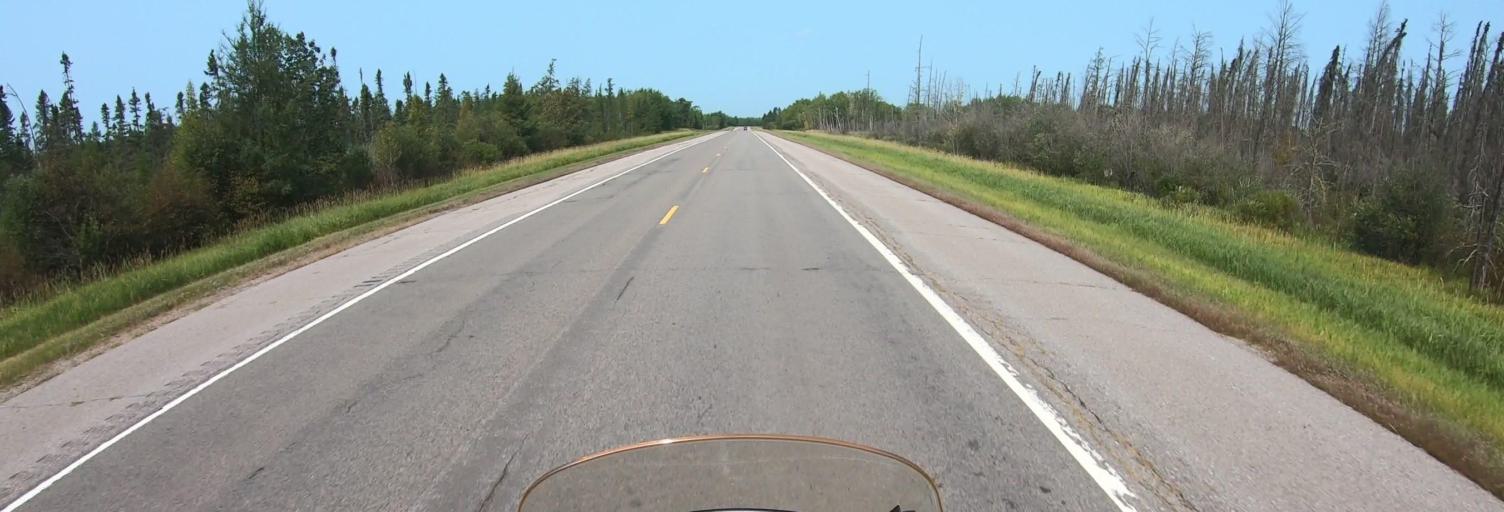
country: US
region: Minnesota
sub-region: Saint Louis County
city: Mountain Iron
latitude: 47.8695
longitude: -92.7437
